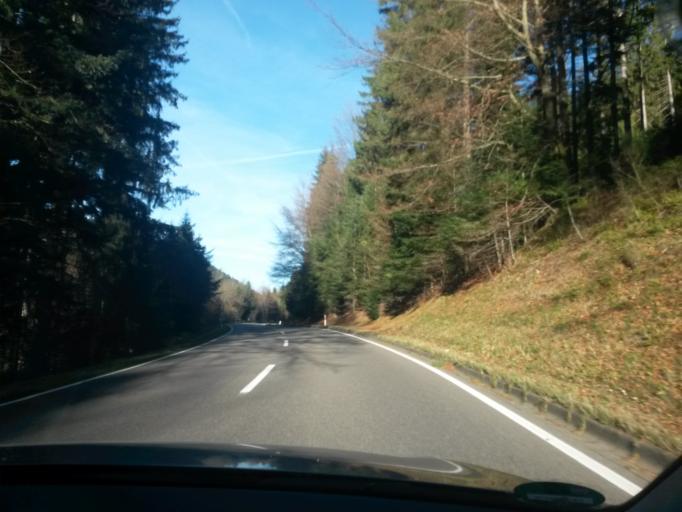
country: DE
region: Baden-Wuerttemberg
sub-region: Karlsruhe Region
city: Bad Wildbad
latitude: 48.7297
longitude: 8.5730
